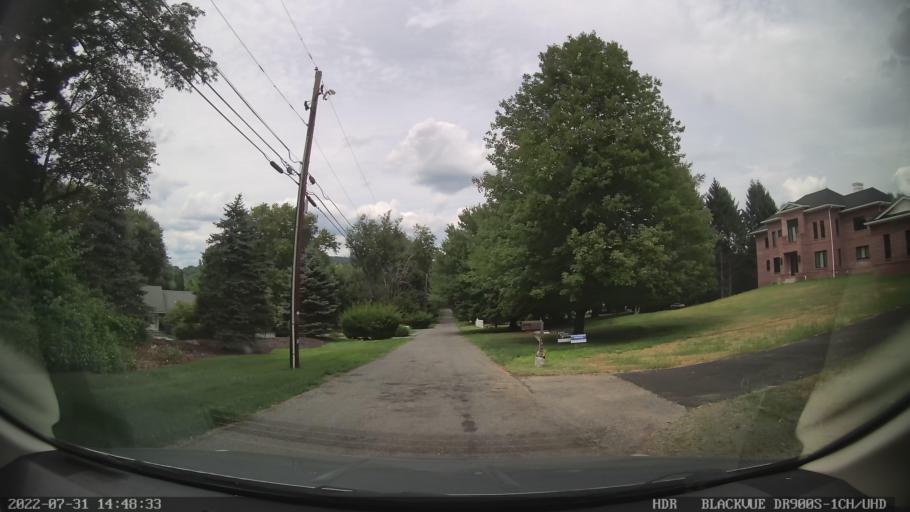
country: US
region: Pennsylvania
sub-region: Northampton County
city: Hellertown
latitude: 40.5732
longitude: -75.3648
